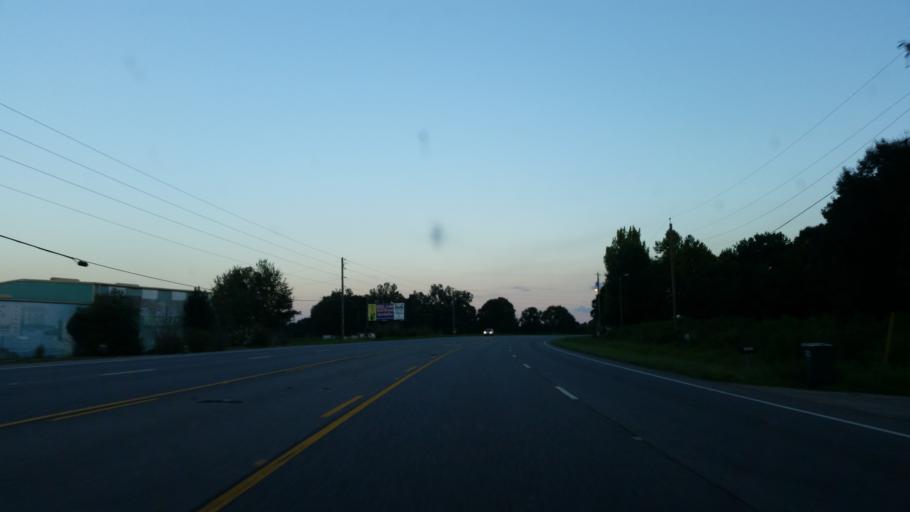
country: US
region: Alabama
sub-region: Baldwin County
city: Loxley
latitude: 30.6067
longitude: -87.7412
